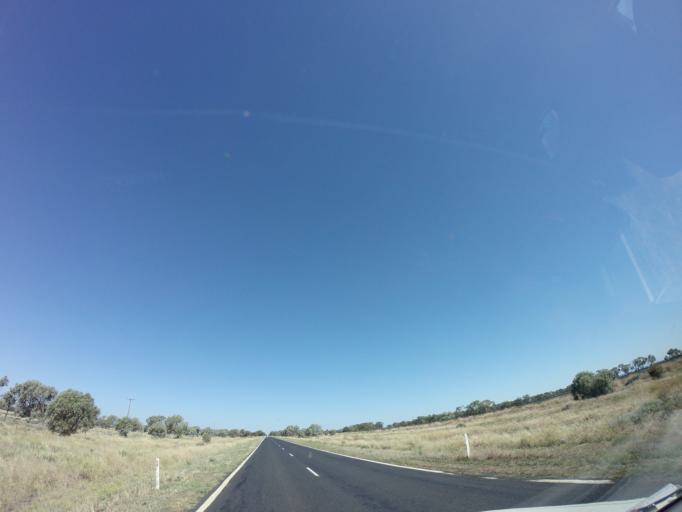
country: AU
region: New South Wales
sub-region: Bogan
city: Nyngan
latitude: -31.7777
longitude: 147.6038
